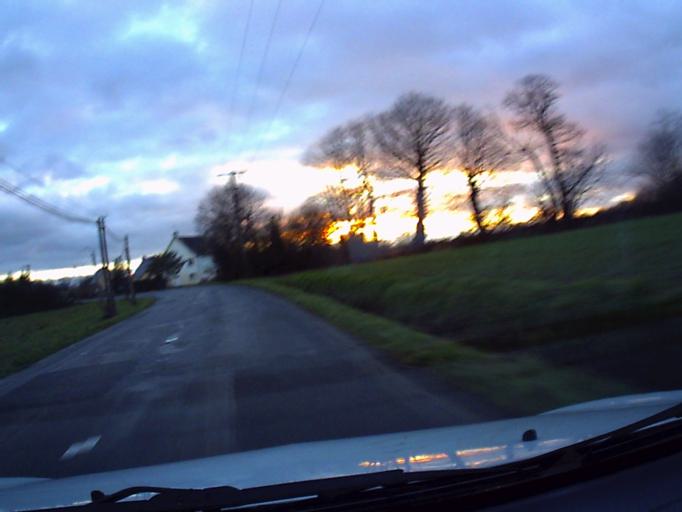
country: FR
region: Brittany
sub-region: Departement d'Ille-et-Vilaine
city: Iffendic
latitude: 48.1242
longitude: -2.0395
